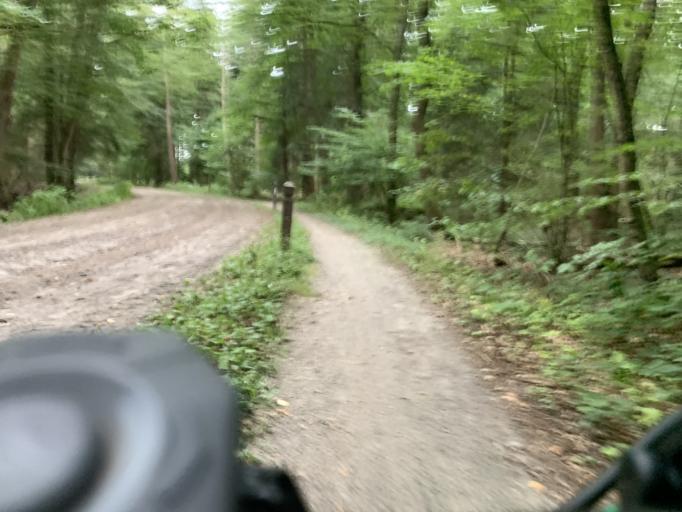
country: DE
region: Lower Saxony
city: Westerstede
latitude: 53.2325
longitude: 7.9307
